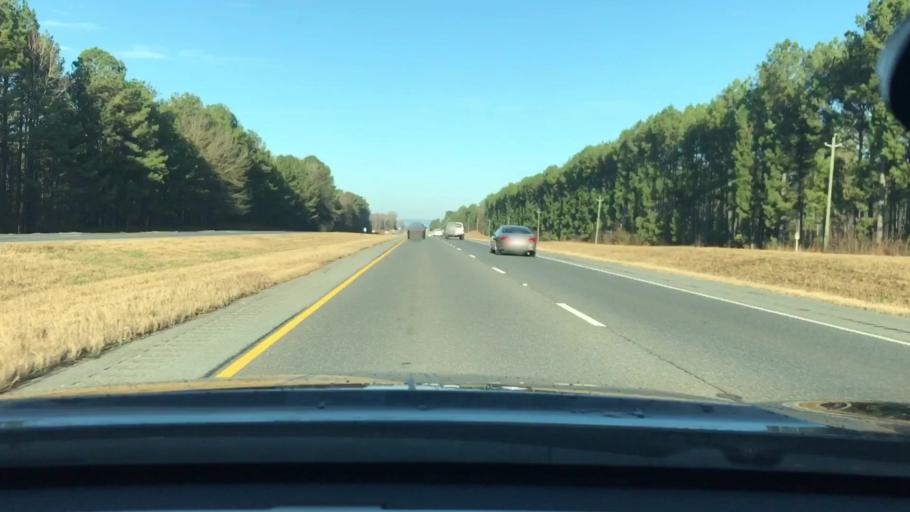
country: US
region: Alabama
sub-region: Talladega County
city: Childersburg
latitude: 33.3063
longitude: -86.3773
